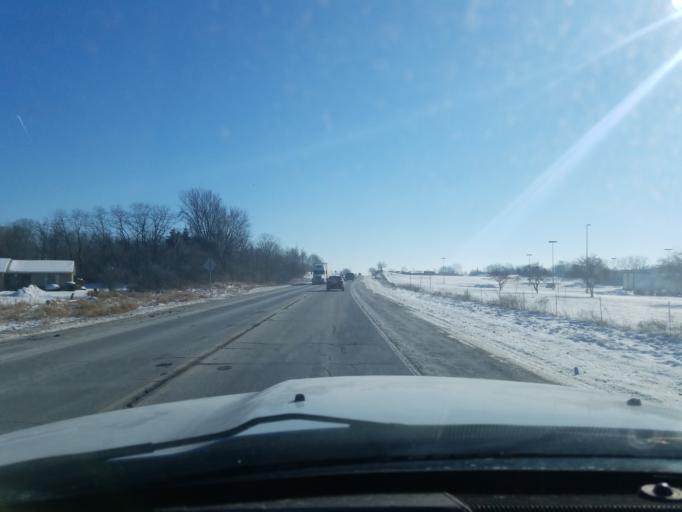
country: US
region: Indiana
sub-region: Noble County
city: Kendallville
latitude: 41.4508
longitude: -85.2445
